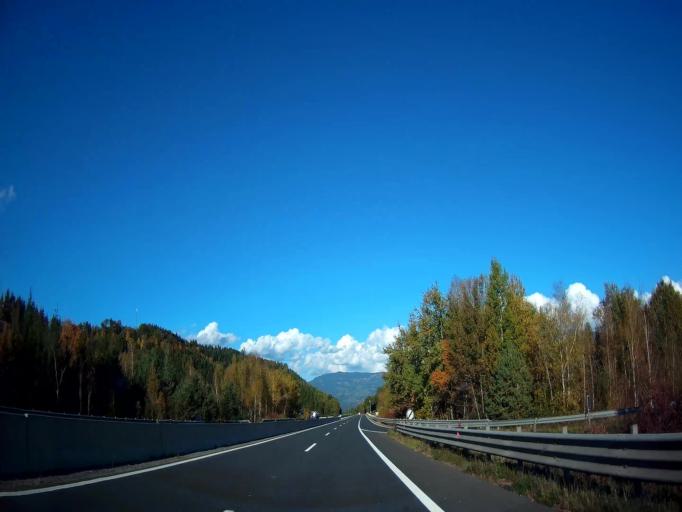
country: AT
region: Carinthia
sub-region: Politischer Bezirk Wolfsberg
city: Sankt Andrae
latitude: 46.7445
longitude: 14.8085
